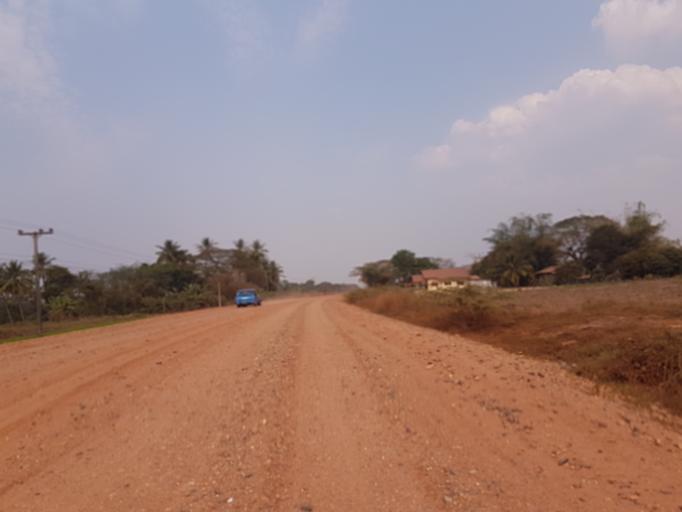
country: TH
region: Nong Khai
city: Nong Khai
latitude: 17.9769
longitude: 102.8611
